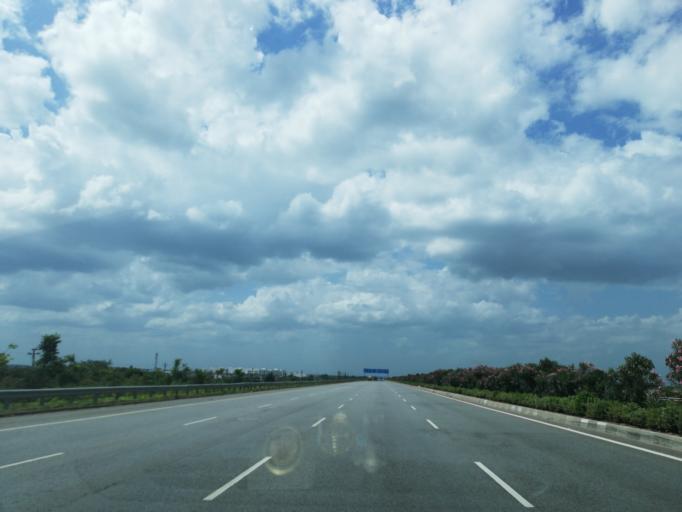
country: IN
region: Telangana
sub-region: Medak
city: Serilingampalle
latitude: 17.4392
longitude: 78.2594
